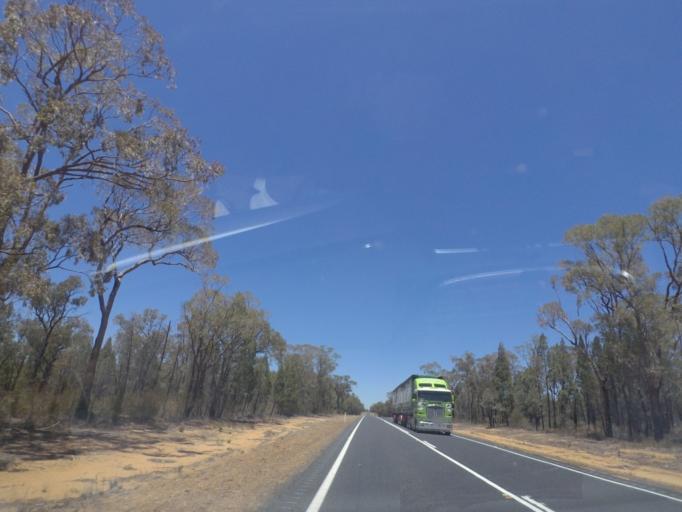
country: AU
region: New South Wales
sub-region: Narrabri
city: Narrabri
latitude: -30.7359
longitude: 149.5180
